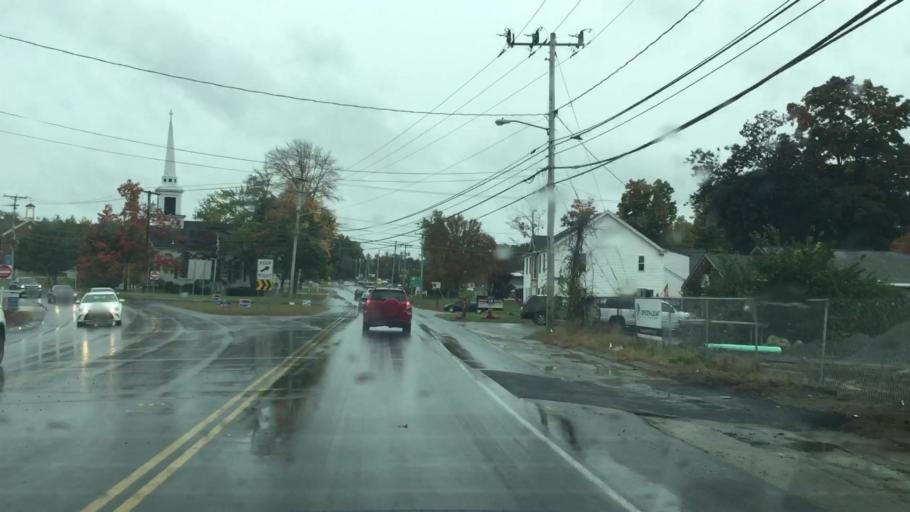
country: US
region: New Hampshire
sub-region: Rockingham County
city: Seabrook
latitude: 42.8778
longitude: -70.8704
